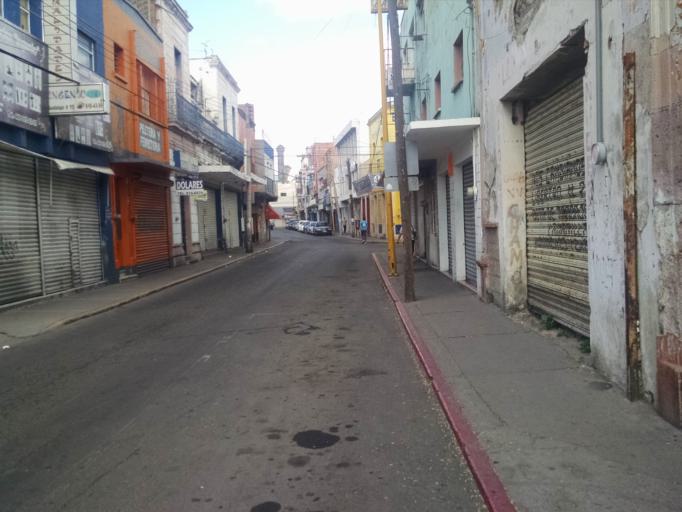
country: MX
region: Aguascalientes
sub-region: Aguascalientes
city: Aguascalientes
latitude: 21.8834
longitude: -102.2995
